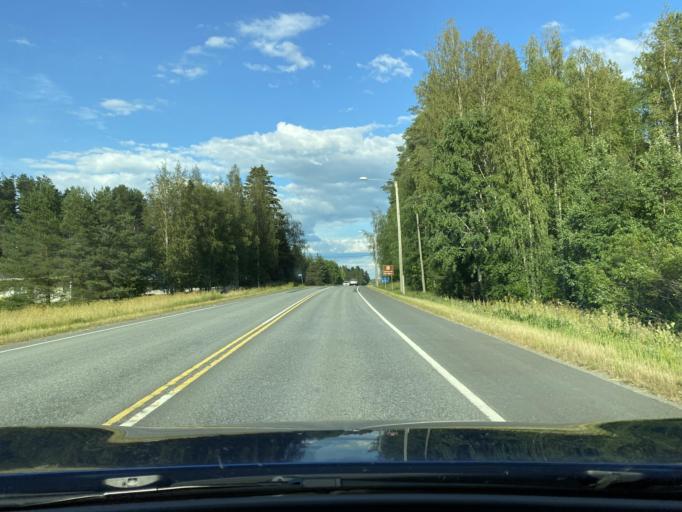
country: FI
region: Southern Ostrobothnia
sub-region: Jaerviseutu
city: Alajaervi
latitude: 63.0153
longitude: 23.6337
